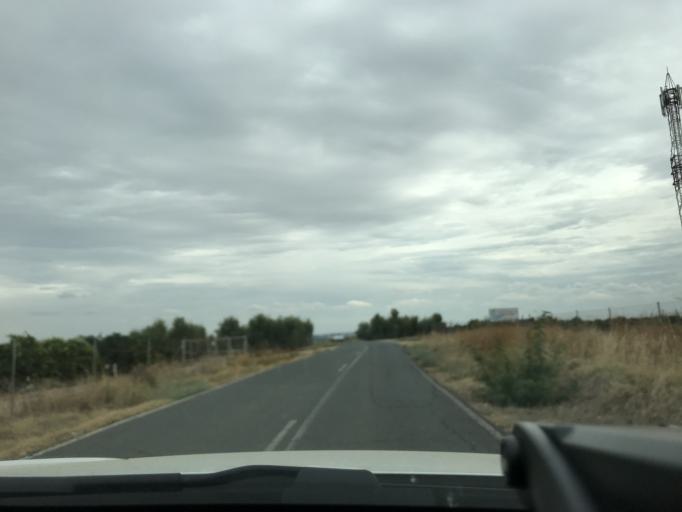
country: ES
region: Andalusia
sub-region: Provincia de Sevilla
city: Villanueva del Rio y Minas
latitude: 37.6399
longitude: -5.7036
